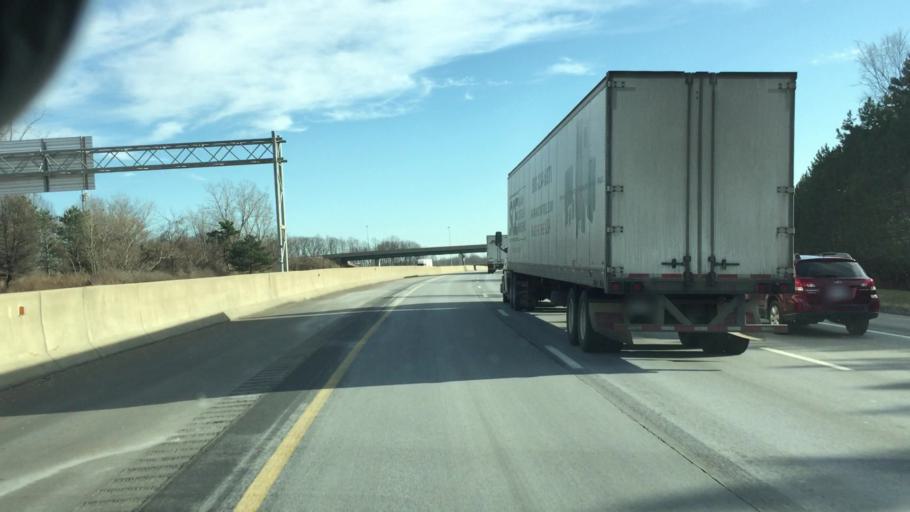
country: US
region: Ohio
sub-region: Cuyahoga County
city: Middleburg Heights
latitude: 41.3397
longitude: -81.8256
